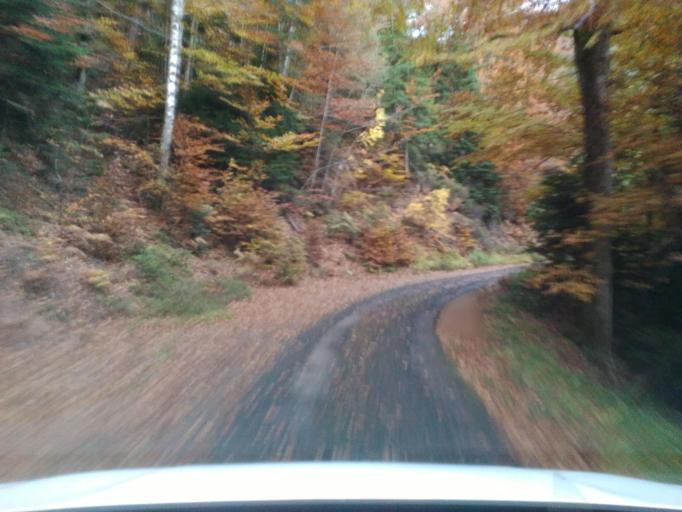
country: FR
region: Lorraine
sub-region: Departement des Vosges
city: Sainte-Marguerite
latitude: 48.3063
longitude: 6.9863
